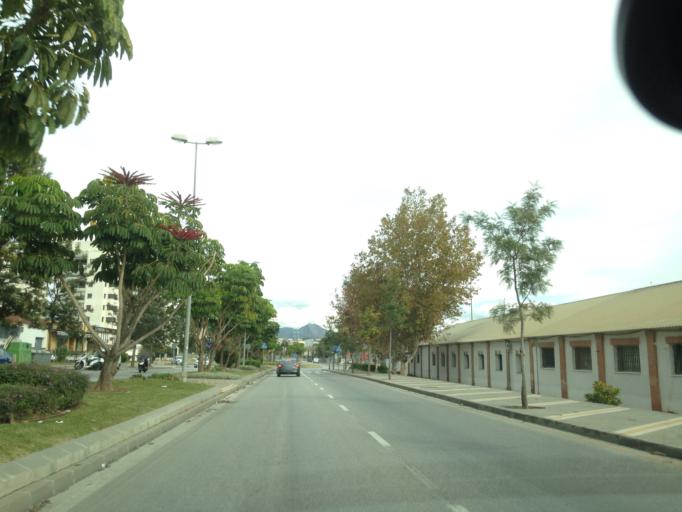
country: ES
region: Andalusia
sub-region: Provincia de Malaga
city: Malaga
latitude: 36.7039
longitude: -4.4554
